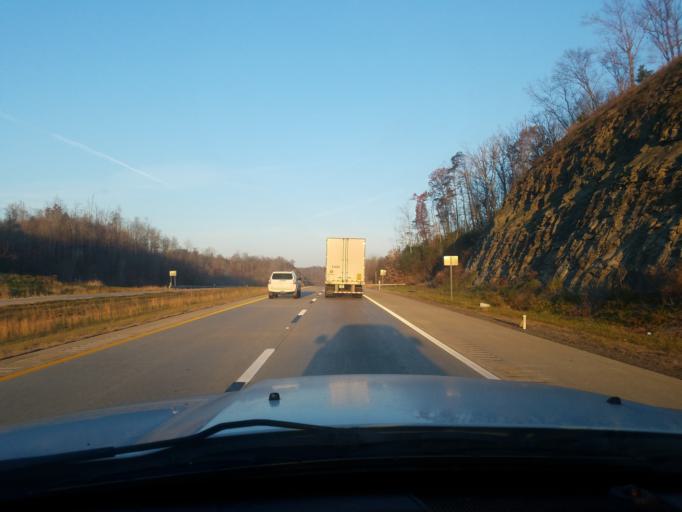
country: US
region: West Virginia
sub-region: Putnam County
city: Eleanor
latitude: 38.5278
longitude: -81.9424
